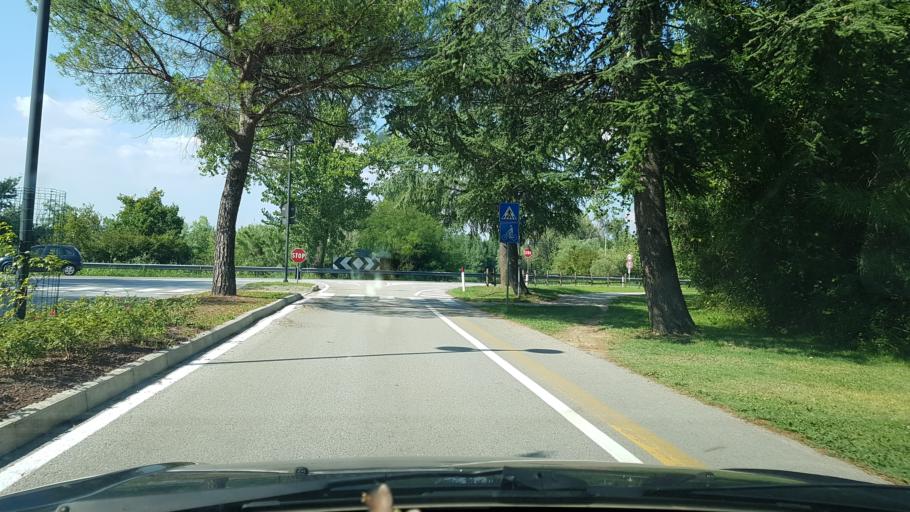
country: IT
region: Friuli Venezia Giulia
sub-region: Provincia di Gorizia
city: Monfalcone
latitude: 45.7830
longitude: 13.5233
